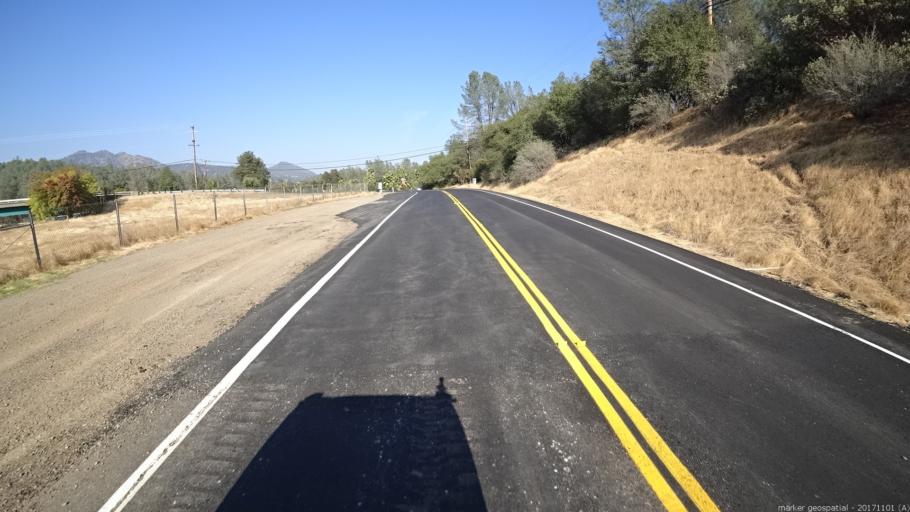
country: US
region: California
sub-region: Shasta County
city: Shasta Lake
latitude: 40.6824
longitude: -122.3467
